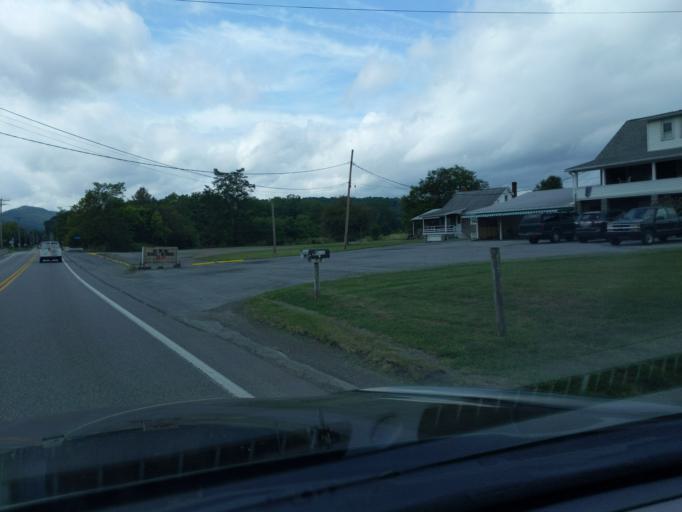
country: US
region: Pennsylvania
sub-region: Blair County
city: Duncansville
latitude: 40.3926
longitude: -78.4124
